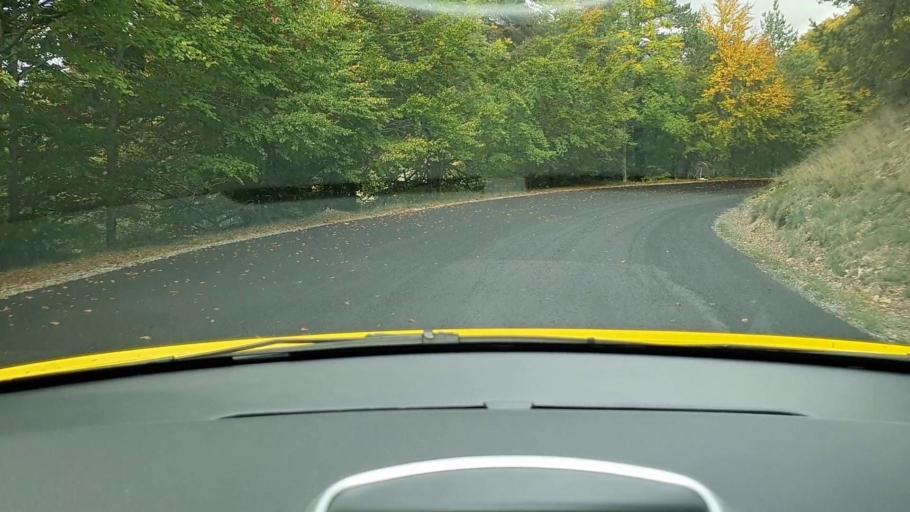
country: FR
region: Languedoc-Roussillon
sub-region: Departement du Gard
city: Valleraugue
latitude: 44.0778
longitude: 3.5321
